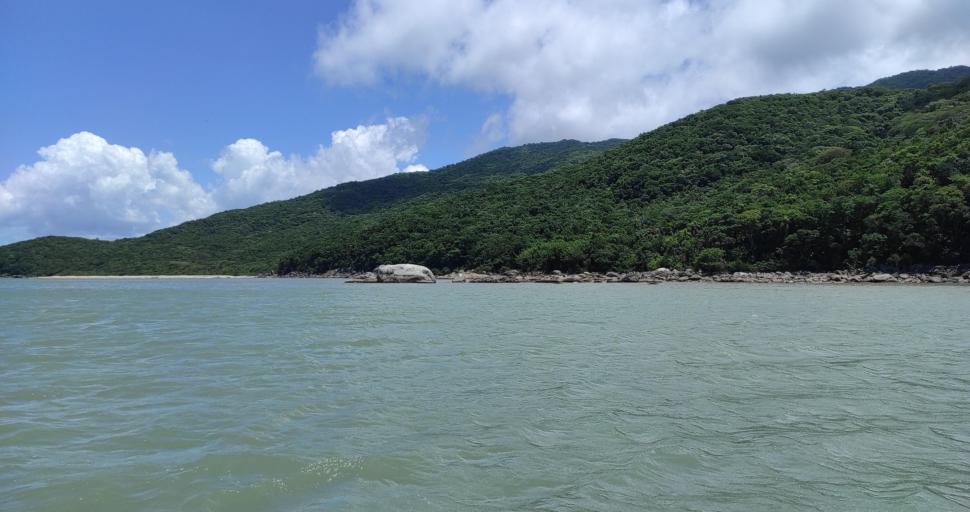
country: BR
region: Santa Catarina
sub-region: Porto Belo
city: Porto Belo
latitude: -27.2003
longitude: -48.5612
